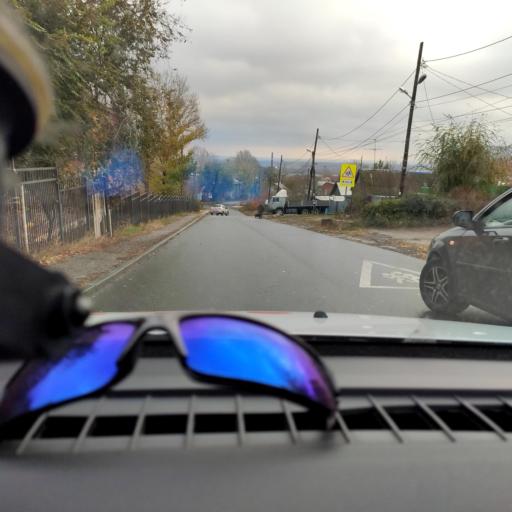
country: RU
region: Samara
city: Samara
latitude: 53.1820
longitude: 50.1998
